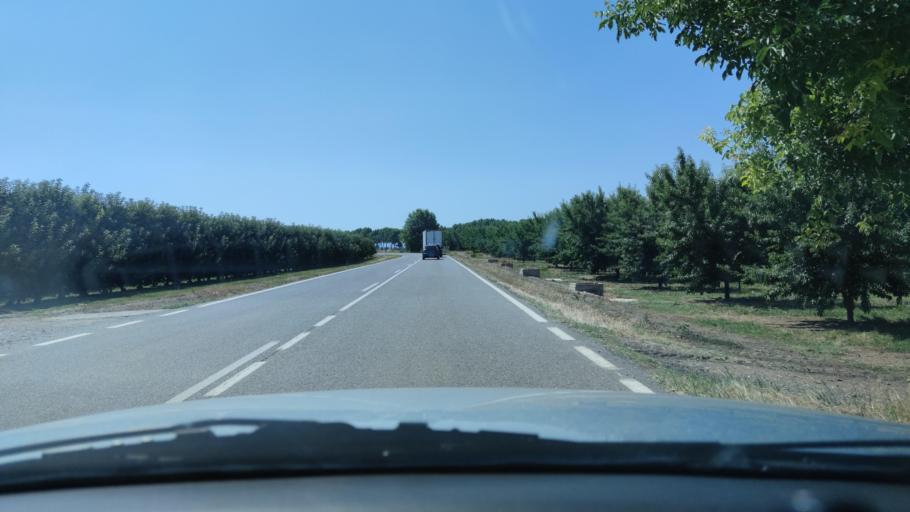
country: ES
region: Catalonia
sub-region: Provincia de Lleida
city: Ivars d'Urgell
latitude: 41.6951
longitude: 0.9860
